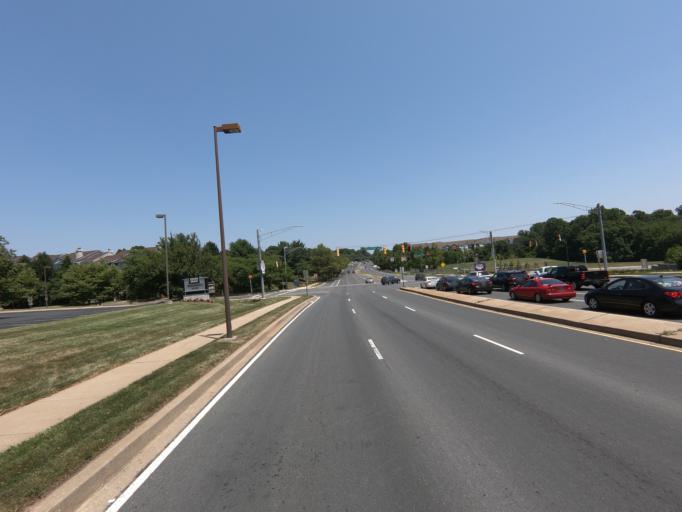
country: US
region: Maryland
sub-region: Montgomery County
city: Germantown
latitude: 39.1906
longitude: -77.2485
